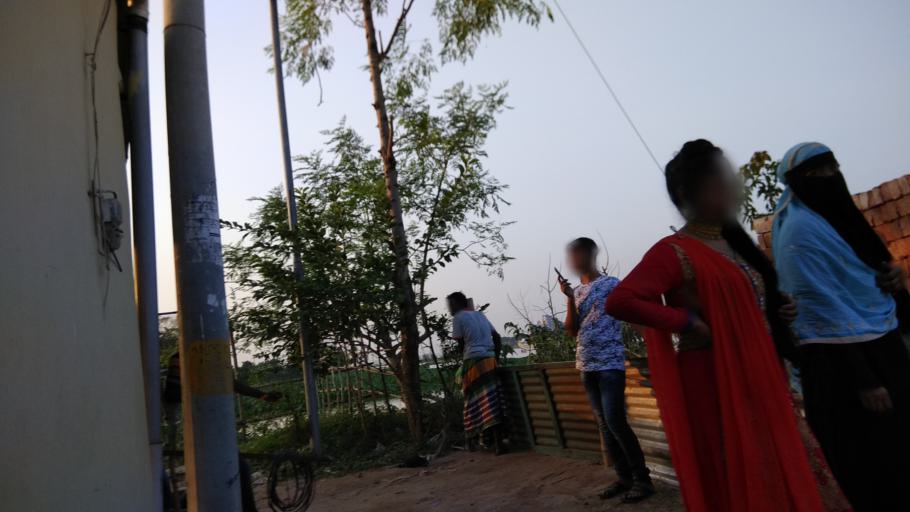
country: BD
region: Dhaka
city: Azimpur
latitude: 23.8007
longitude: 90.3417
